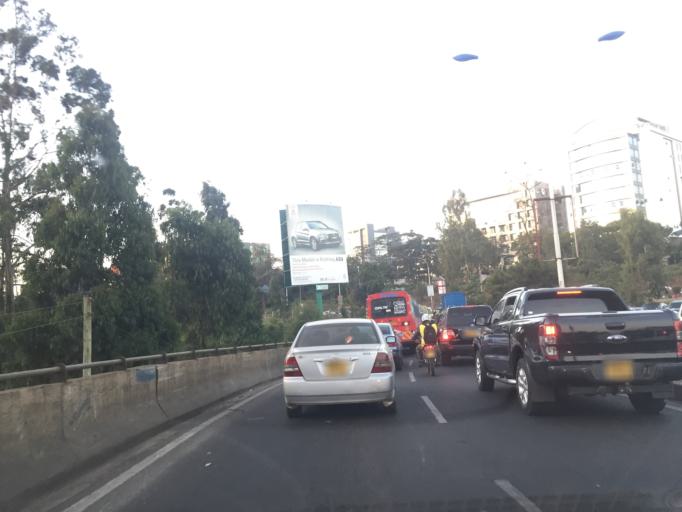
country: KE
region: Nairobi Area
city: Nairobi
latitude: -1.2748
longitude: 36.8105
